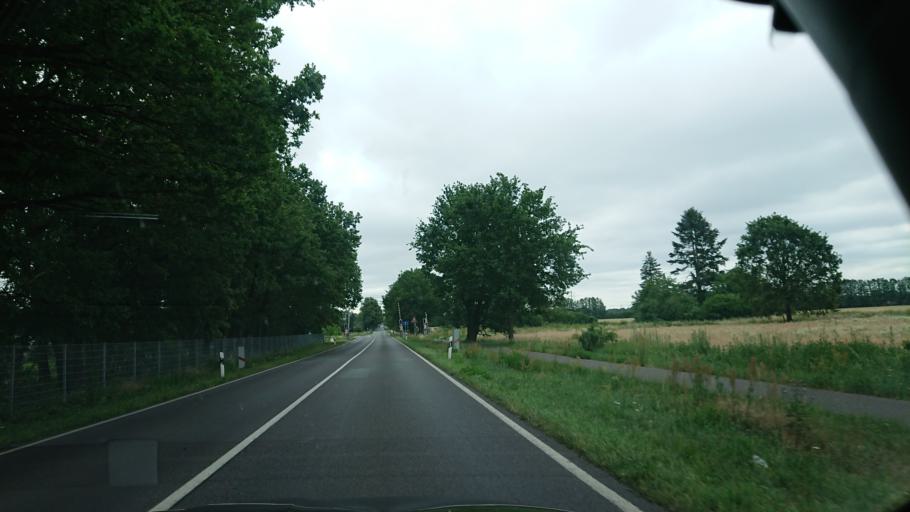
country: DE
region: Brandenburg
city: Perleberg
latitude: 53.0684
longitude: 11.8818
